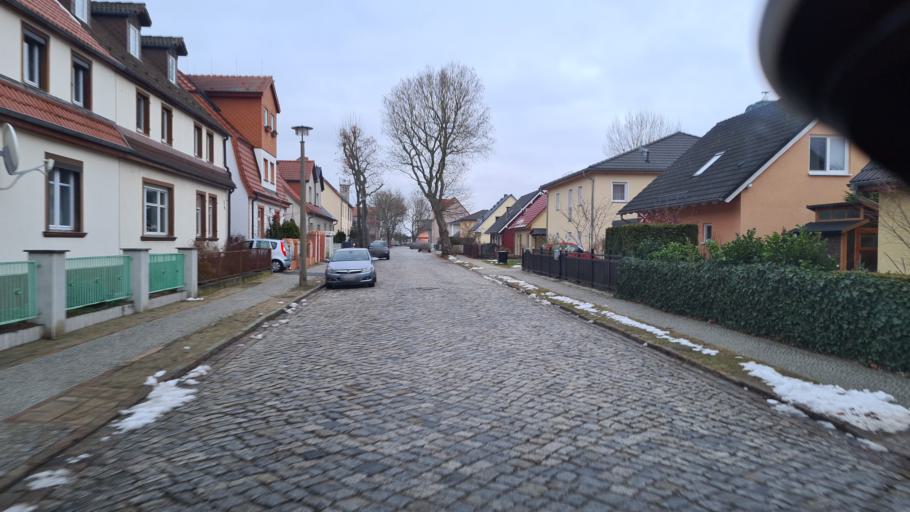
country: DE
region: Brandenburg
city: Eisenhuettenstadt
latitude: 52.1448
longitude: 14.6621
